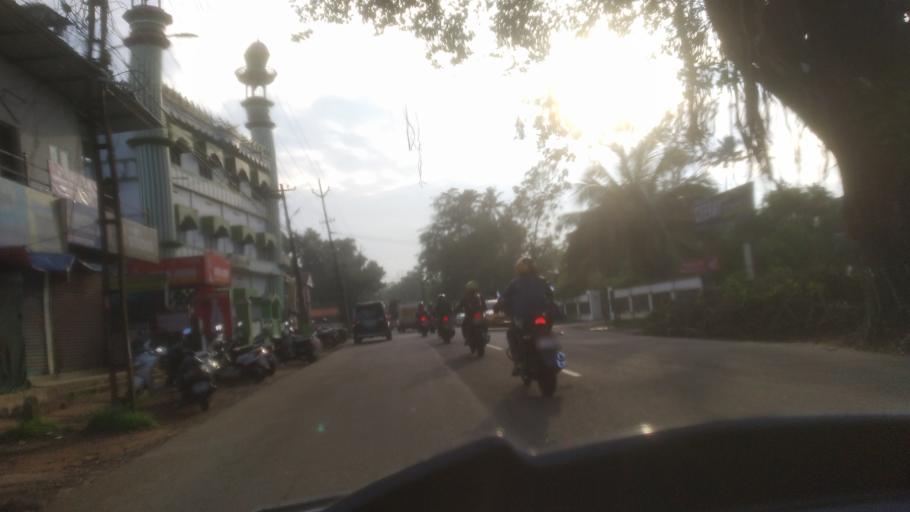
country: IN
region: Kerala
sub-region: Ernakulam
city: Perumpavur
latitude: 10.1167
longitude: 76.4919
